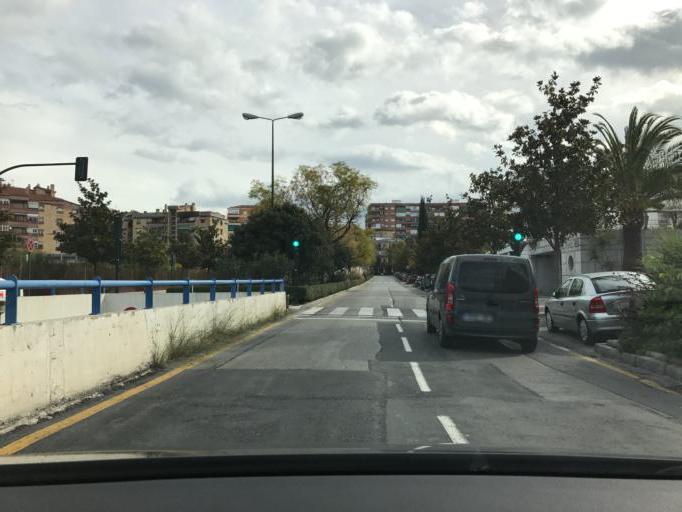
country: ES
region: Andalusia
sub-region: Provincia de Granada
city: Armilla
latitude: 37.1607
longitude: -3.6043
